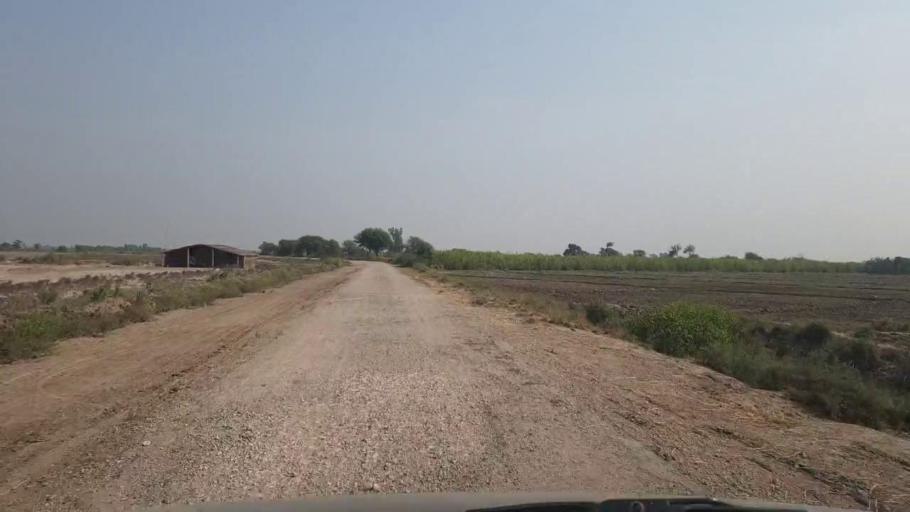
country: PK
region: Sindh
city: Tando Muhammad Khan
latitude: 25.0522
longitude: 68.3887
